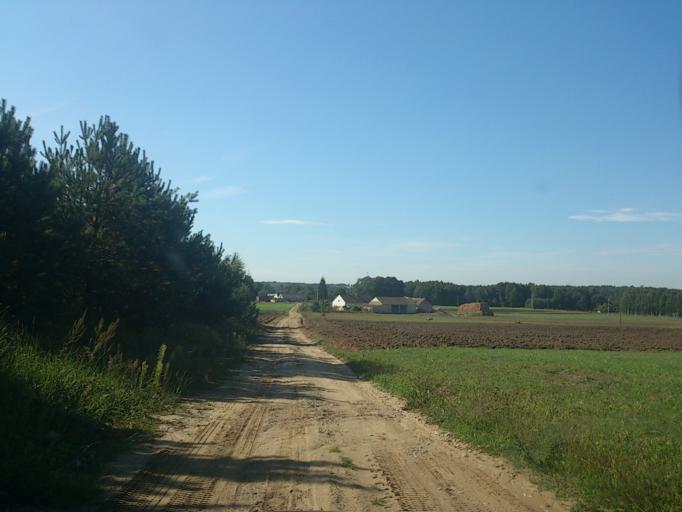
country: PL
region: Kujawsko-Pomorskie
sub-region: Powiat golubsko-dobrzynski
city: Radomin
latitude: 53.1228
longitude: 19.1299
